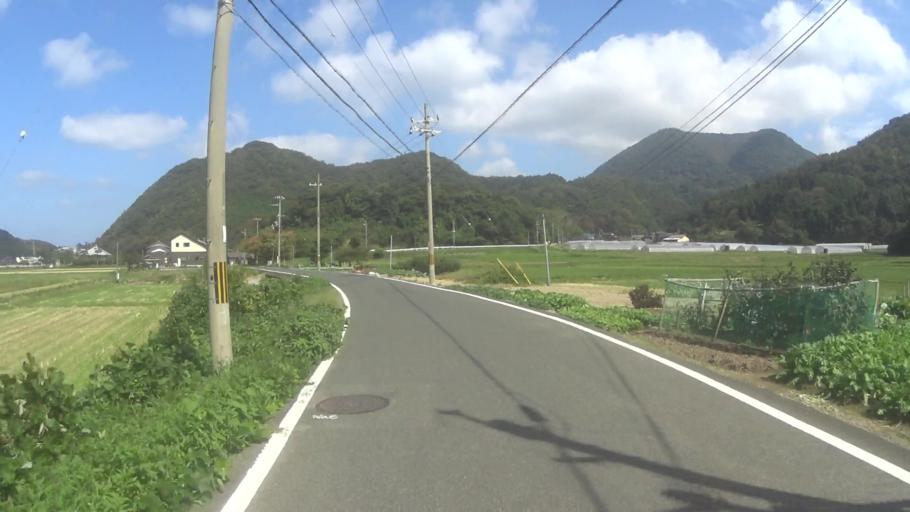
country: JP
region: Kyoto
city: Miyazu
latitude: 35.7333
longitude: 135.1084
